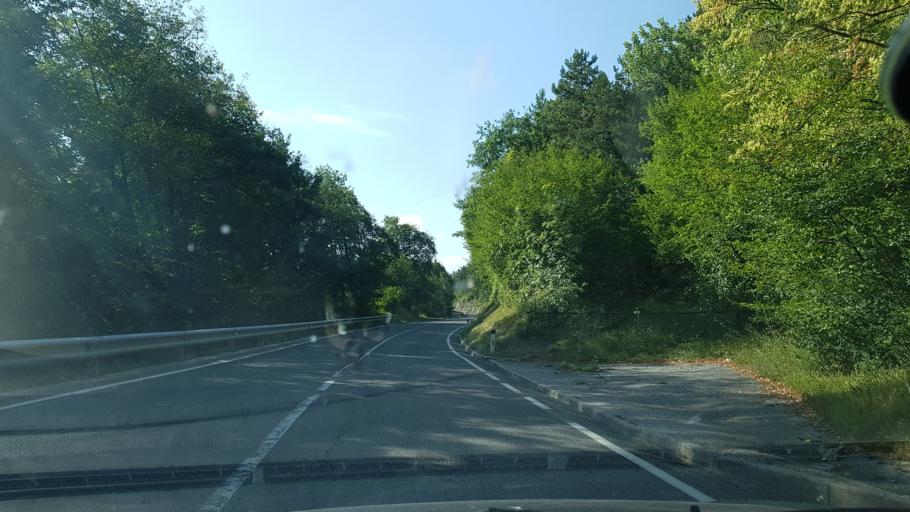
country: SI
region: Nova Gorica
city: Solkan
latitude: 45.9844
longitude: 13.6612
